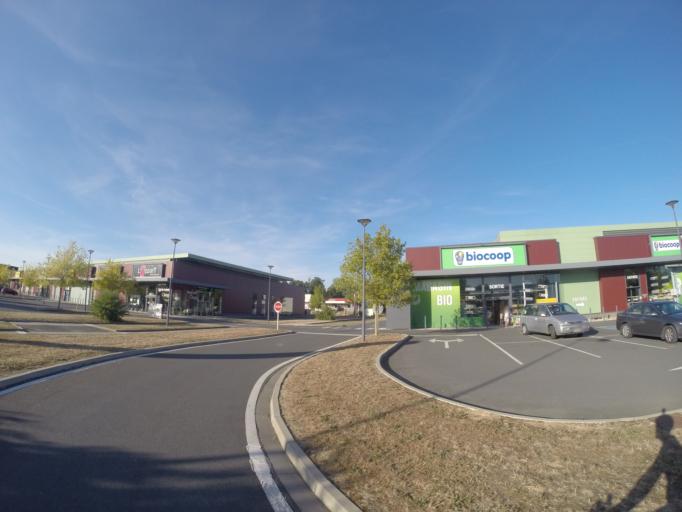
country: FR
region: Centre
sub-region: Departement d'Indre-et-Loire
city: Parcay-Meslay
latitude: 47.4287
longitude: 0.7082
